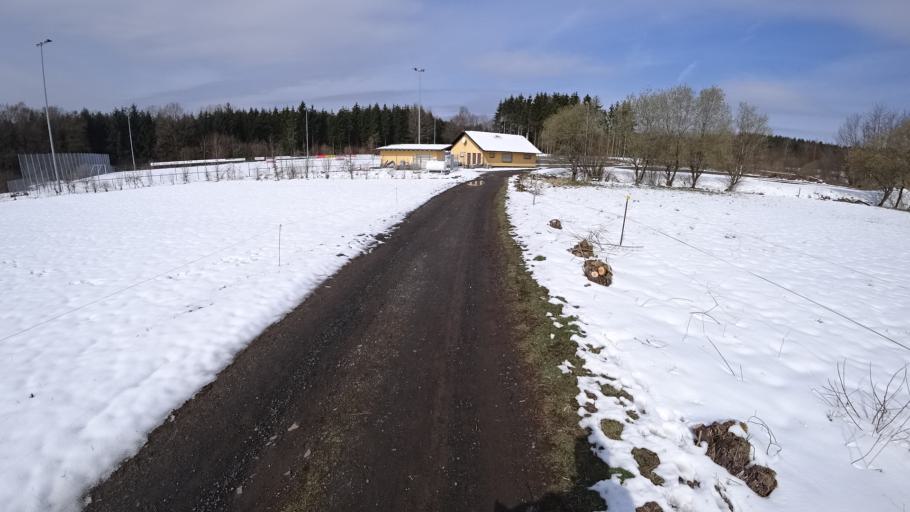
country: DE
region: Rheinland-Pfalz
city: Morlen
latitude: 50.7046
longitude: 7.8836
